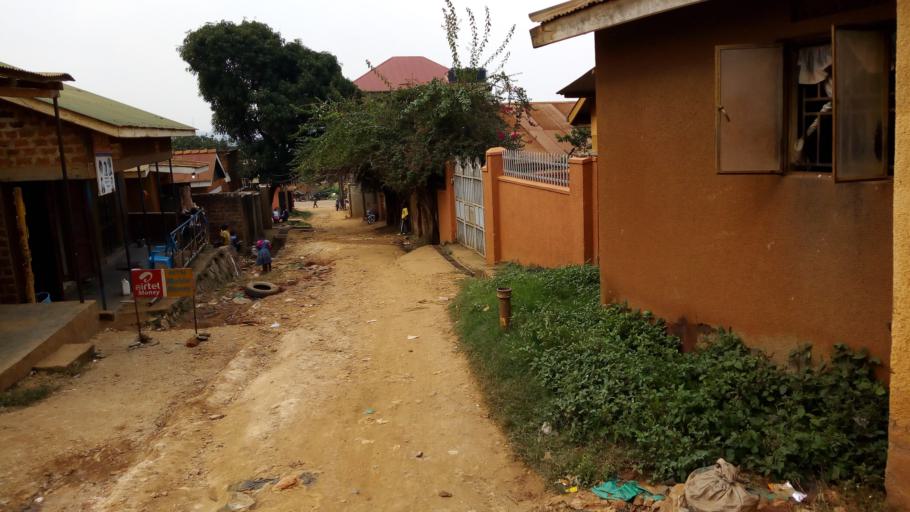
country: UG
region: Central Region
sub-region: Wakiso District
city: Kireka
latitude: 0.3203
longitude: 32.6442
